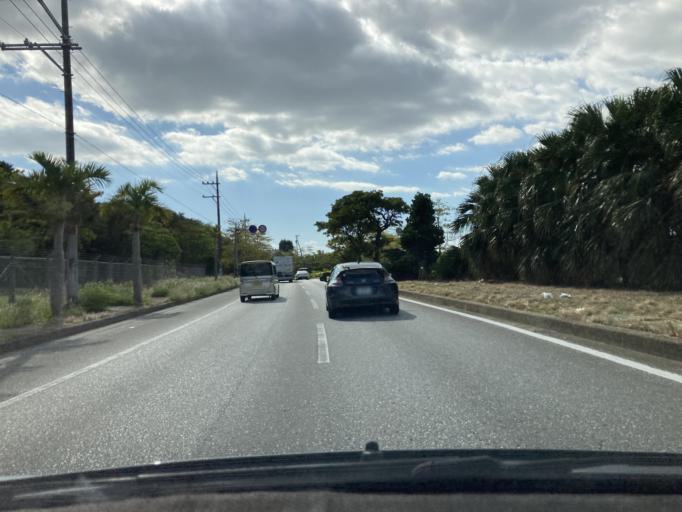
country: JP
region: Okinawa
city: Okinawa
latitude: 26.3194
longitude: 127.7899
